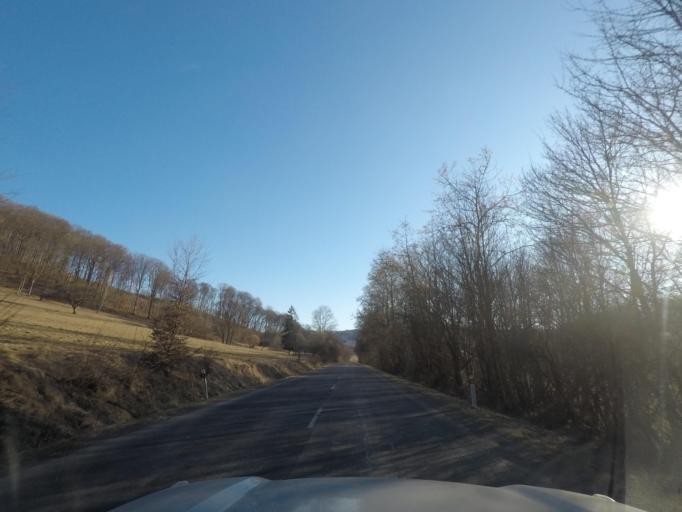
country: SK
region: Presovsky
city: Medzilaborce
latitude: 49.2638
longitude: 21.7971
